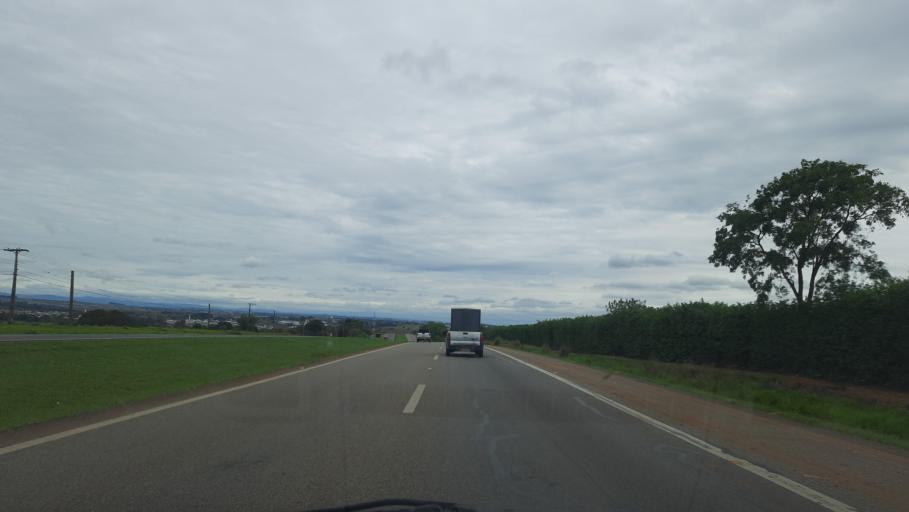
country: BR
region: Sao Paulo
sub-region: Moji-Guacu
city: Mogi-Gaucu
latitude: -22.2560
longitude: -46.9774
